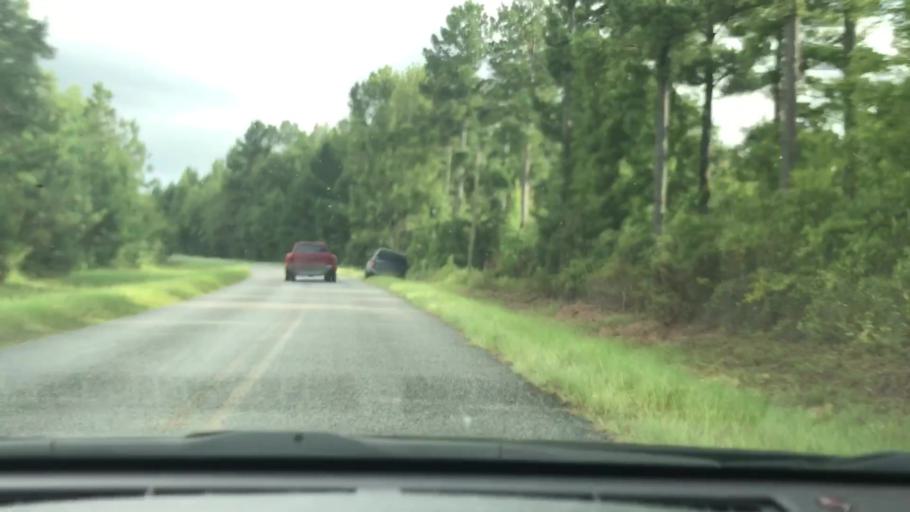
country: US
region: Georgia
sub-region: Jefferson County
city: Wadley
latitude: 32.8130
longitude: -82.3759
